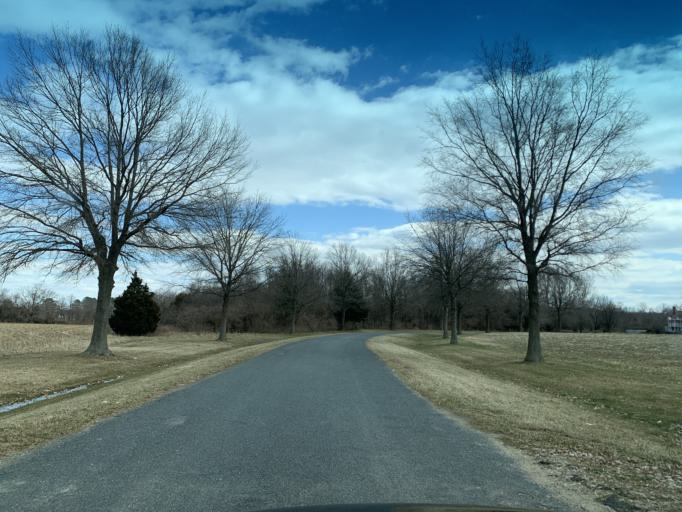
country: US
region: Maryland
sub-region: Queen Anne's County
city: Stevensville
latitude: 38.9665
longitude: -76.3171
